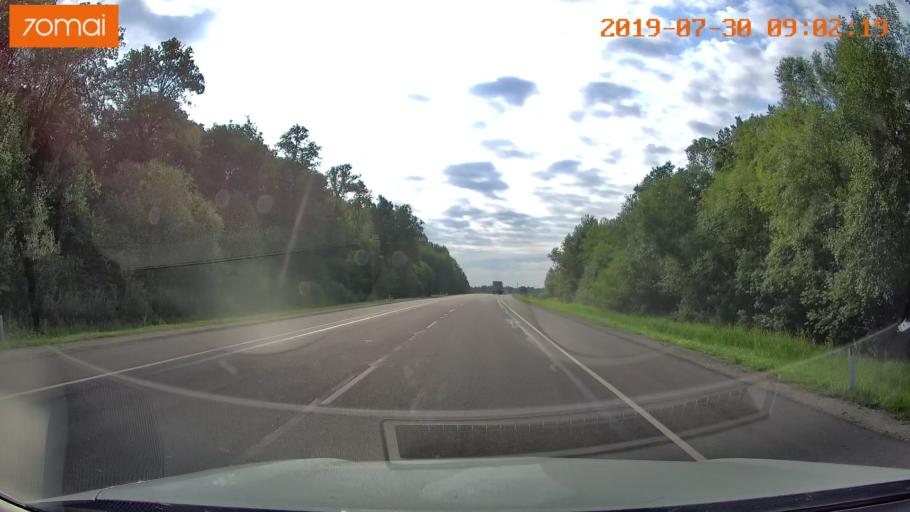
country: RU
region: Kaliningrad
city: Gusev
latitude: 54.6165
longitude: 22.2294
